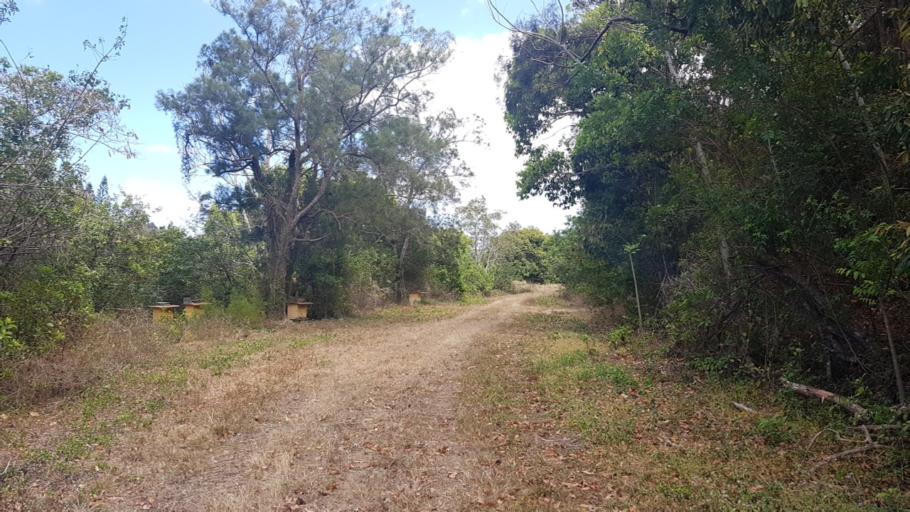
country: NC
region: South Province
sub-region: Dumbea
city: Dumbea
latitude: -22.1761
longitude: 166.4717
